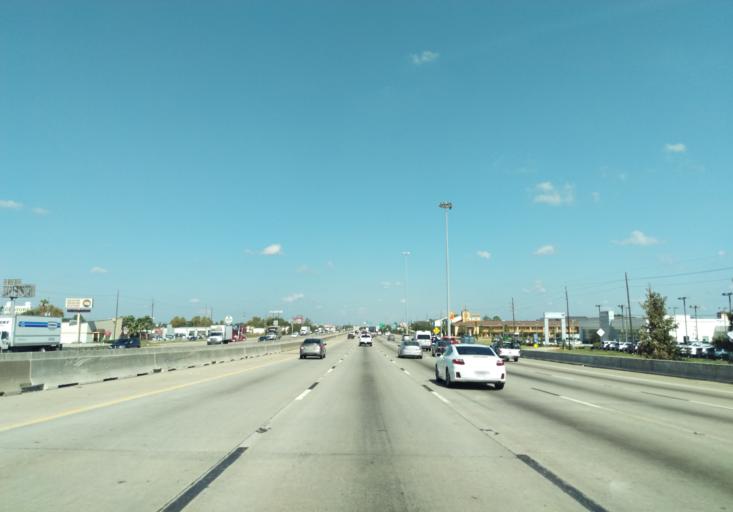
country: US
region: Texas
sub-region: Harris County
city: Spring
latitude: 30.0004
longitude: -95.4260
